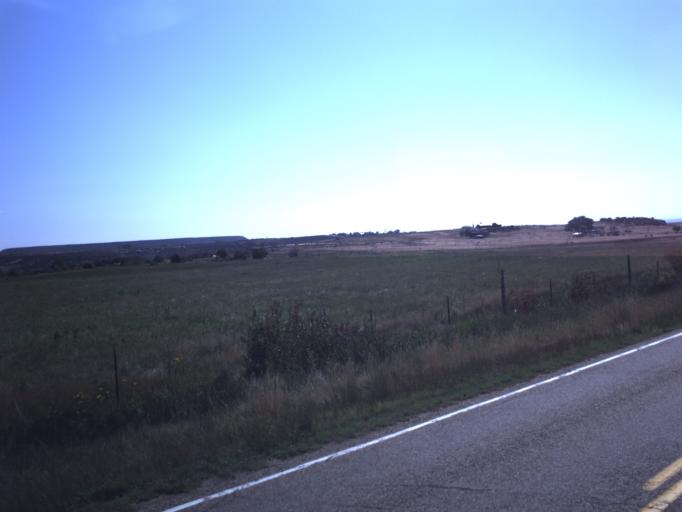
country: US
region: Utah
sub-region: Duchesne County
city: Duchesne
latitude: 40.3093
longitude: -110.2456
